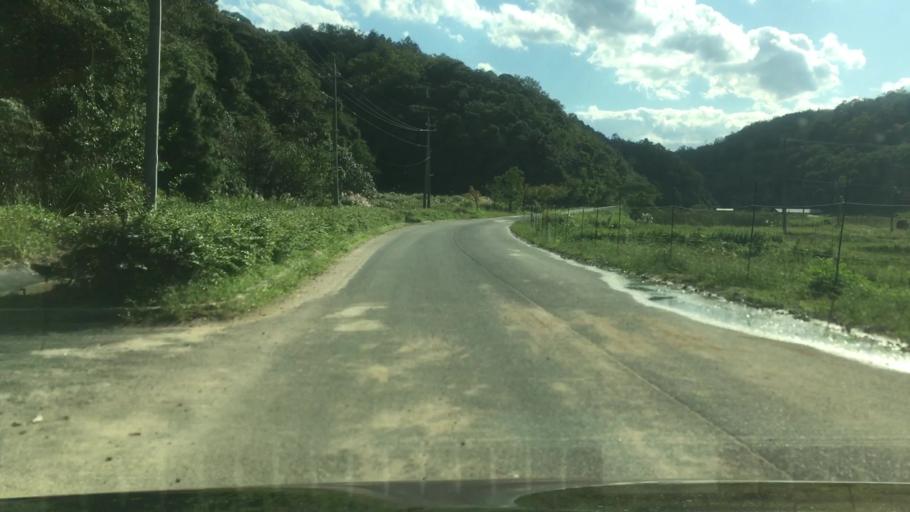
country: JP
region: Hyogo
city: Toyooka
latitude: 35.6471
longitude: 134.9644
